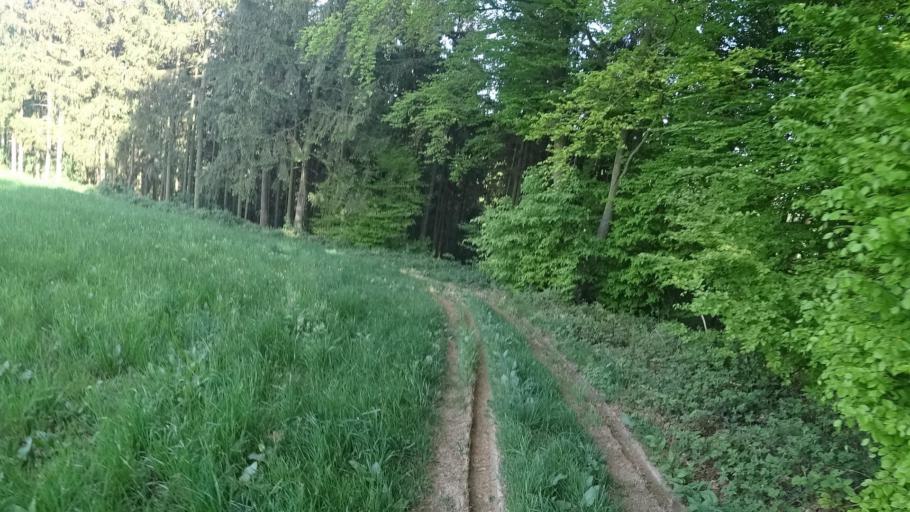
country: DE
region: Rheinland-Pfalz
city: Kirchsahr
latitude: 50.5108
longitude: 6.8739
